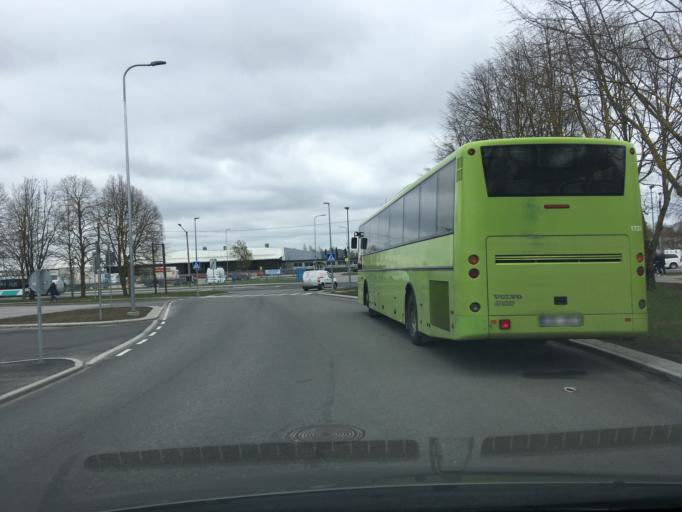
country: EE
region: Harju
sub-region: Tallinna linn
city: Kose
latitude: 59.4355
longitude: 24.8366
